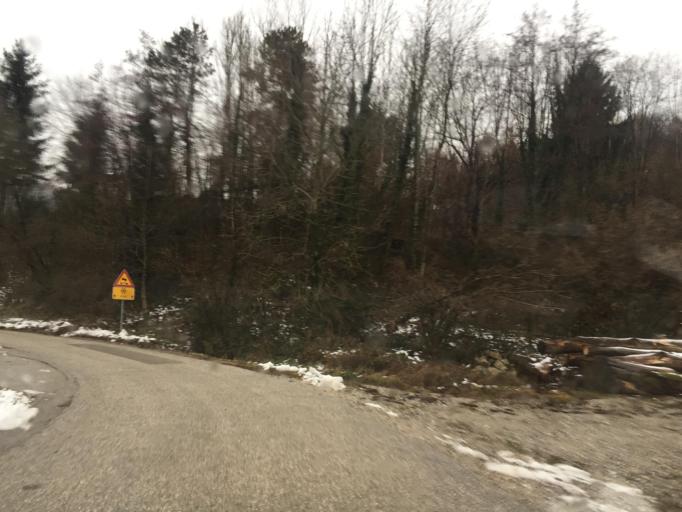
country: SI
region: Kanal
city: Kanal
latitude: 46.0748
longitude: 13.6639
